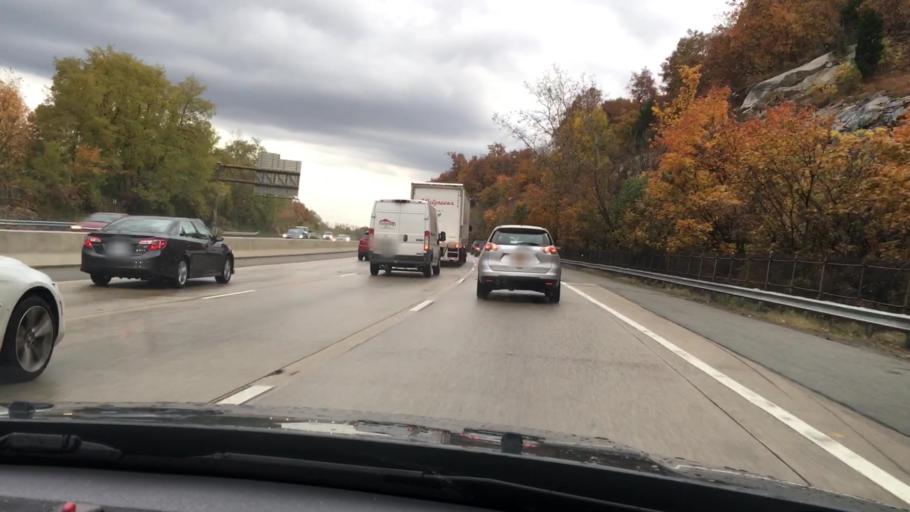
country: US
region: New Jersey
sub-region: Passaic County
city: Pompton Lakes
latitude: 41.0126
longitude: -74.3014
